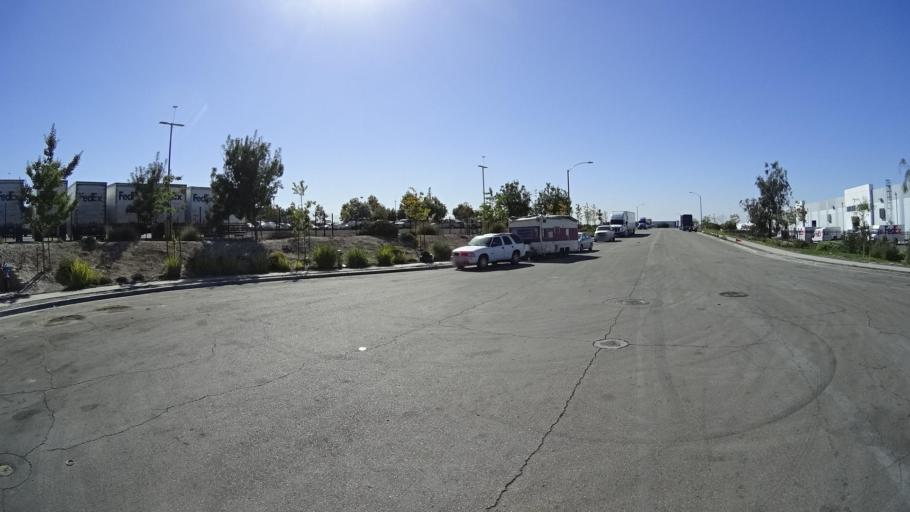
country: MX
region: Baja California
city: Tijuana
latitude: 32.5629
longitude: -116.9343
